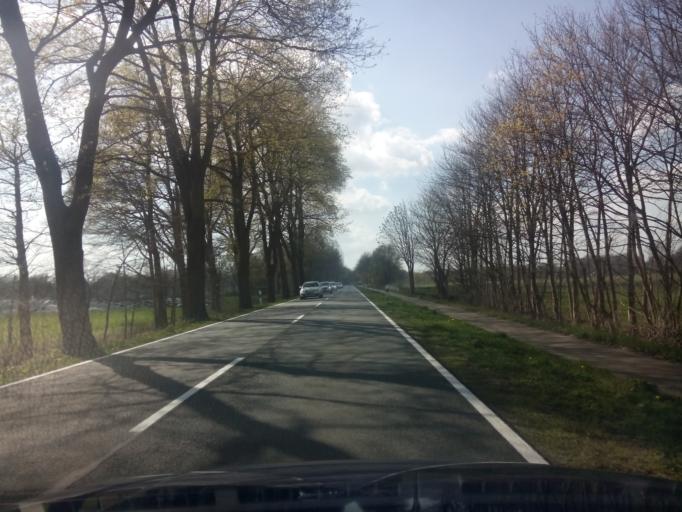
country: DE
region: Lower Saxony
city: Lilienthal
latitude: 53.1810
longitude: 8.8590
